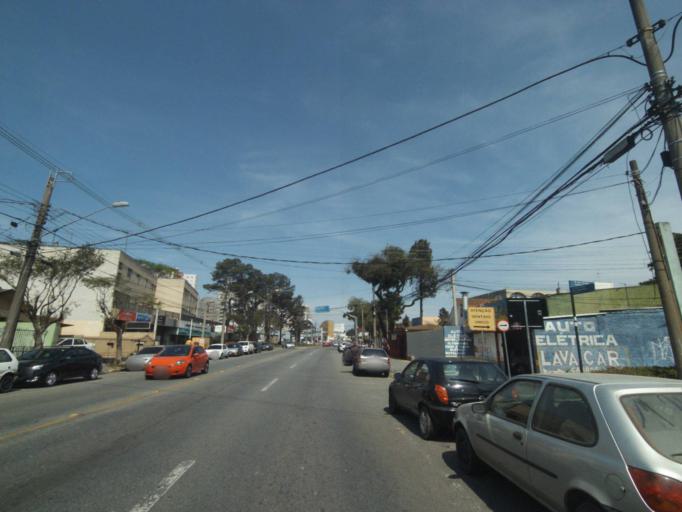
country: BR
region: Parana
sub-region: Curitiba
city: Curitiba
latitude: -25.4689
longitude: -49.2965
